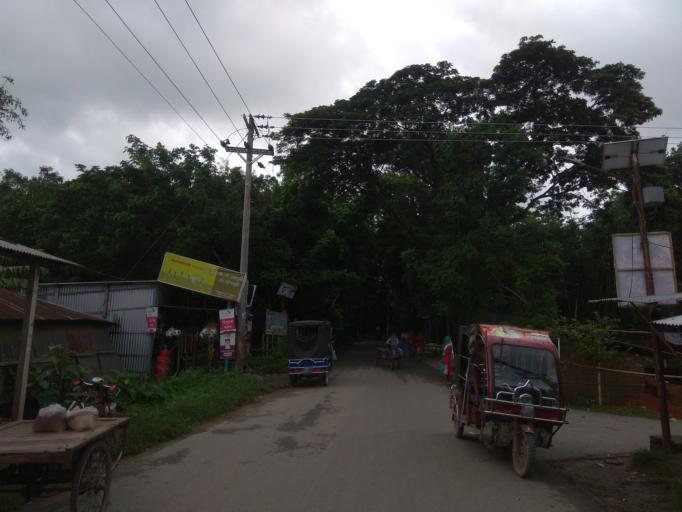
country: BD
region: Dhaka
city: Dohar
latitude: 23.4381
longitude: 90.0738
